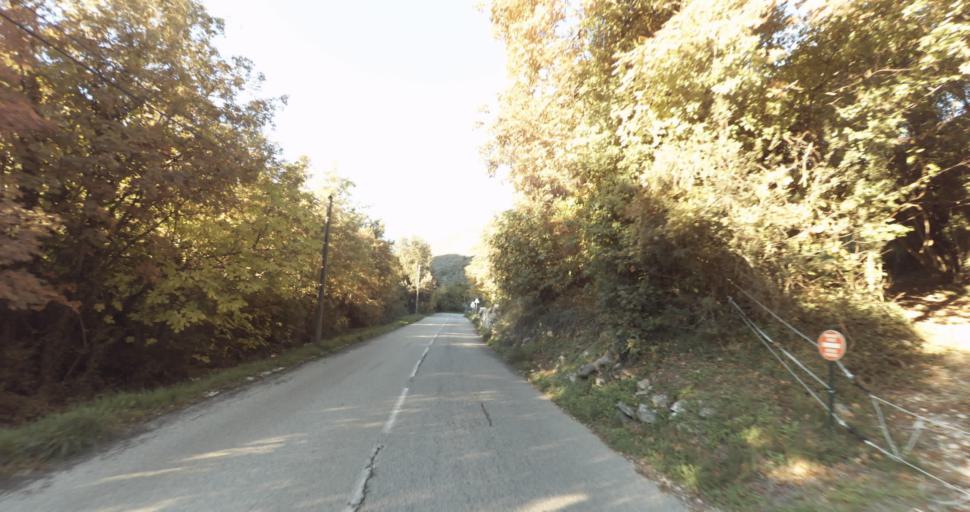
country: FR
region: Provence-Alpes-Cote d'Azur
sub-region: Departement des Alpes-Maritimes
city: Vence
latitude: 43.7396
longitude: 7.1056
